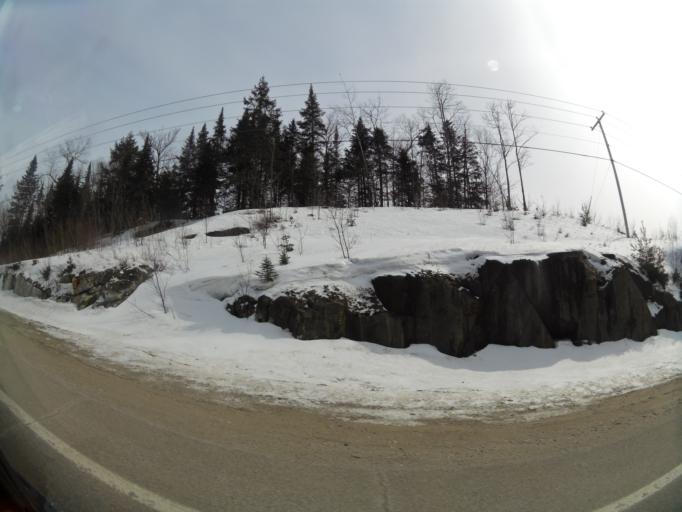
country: CA
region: Quebec
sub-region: Laurentides
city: Mont-Laurier
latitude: 46.2932
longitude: -75.5845
